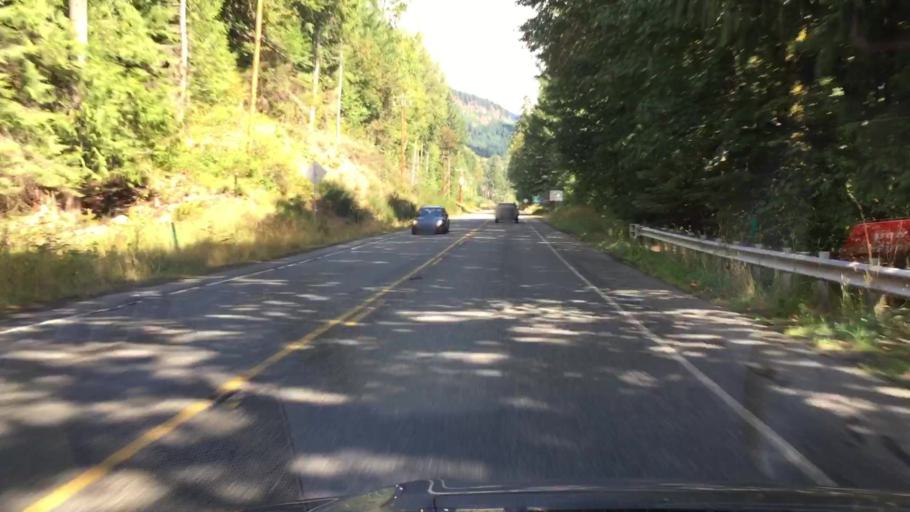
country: US
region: Washington
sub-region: Pierce County
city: Eatonville
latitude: 46.7588
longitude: -122.0483
